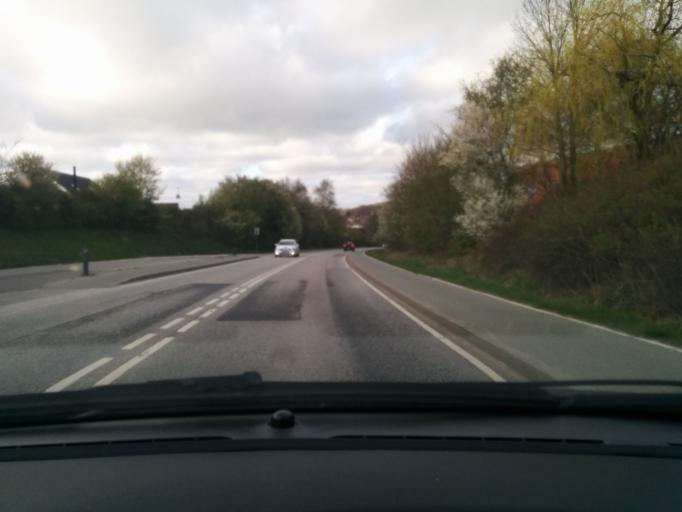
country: DK
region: Central Jutland
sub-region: Favrskov Kommune
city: Hadsten
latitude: 56.3221
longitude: 10.0423
